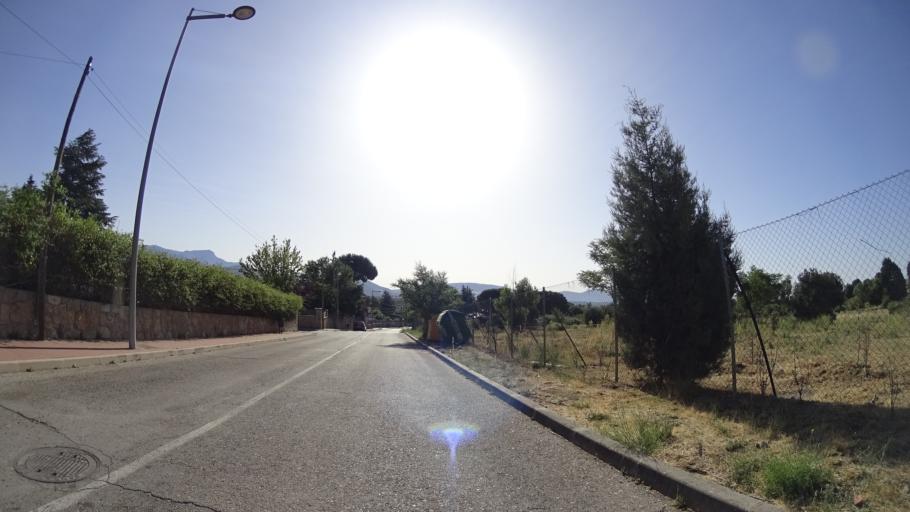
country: ES
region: Madrid
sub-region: Provincia de Madrid
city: Guadarrama
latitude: 40.6800
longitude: -4.1023
